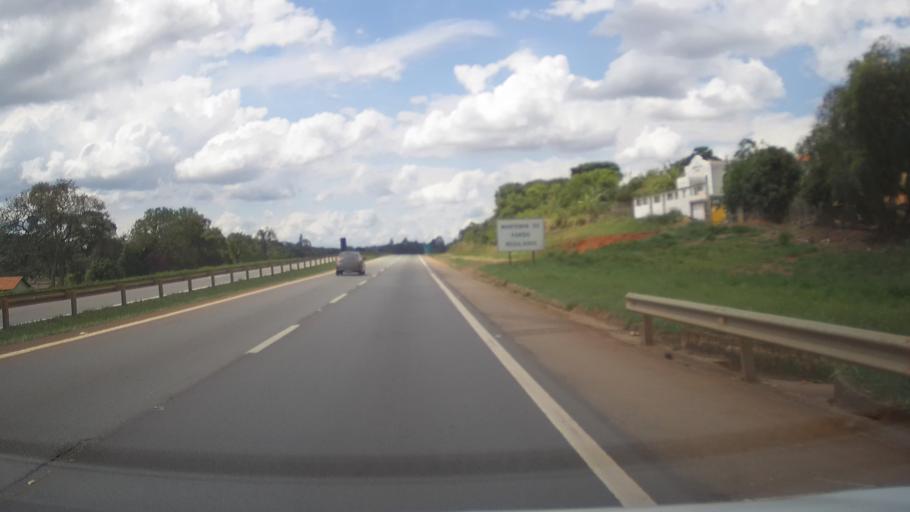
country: BR
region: Minas Gerais
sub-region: Nepomuceno
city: Nepomuceno
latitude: -21.2351
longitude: -45.1347
